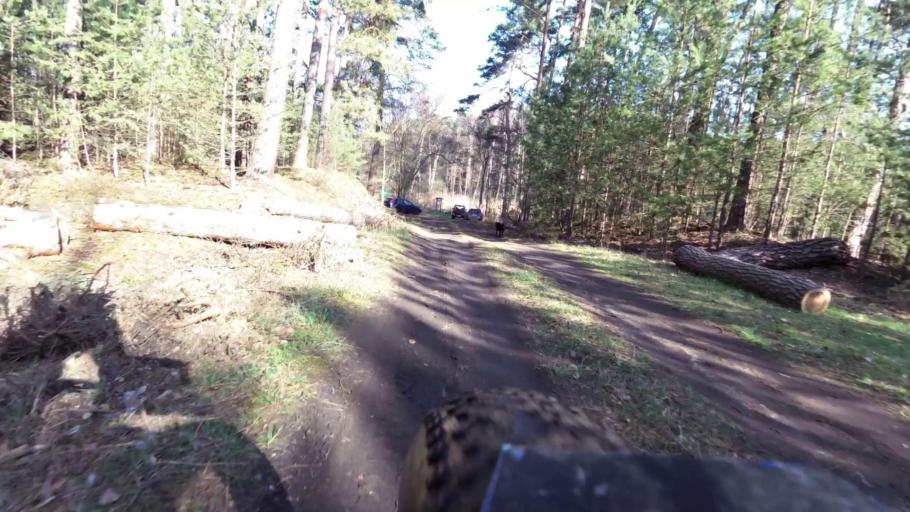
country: PL
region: Lubusz
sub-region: Powiat sulecinski
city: Torzym
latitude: 52.2207
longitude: 15.0051
